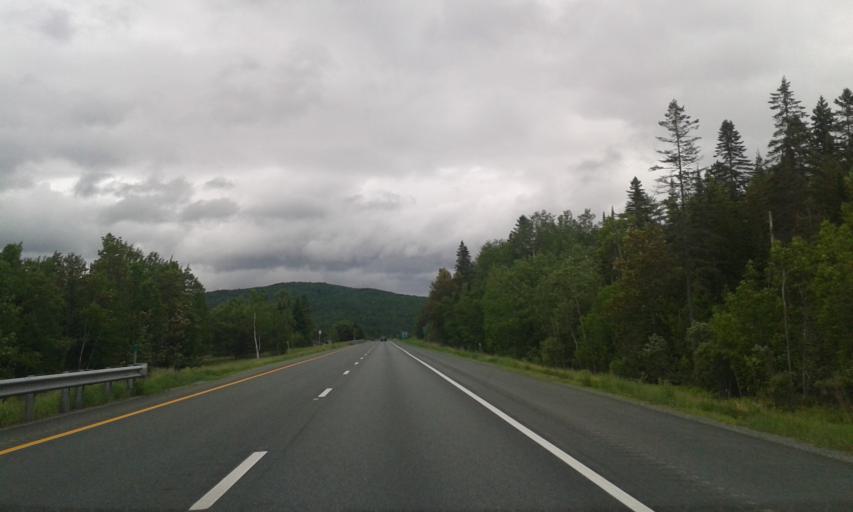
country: US
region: New Hampshire
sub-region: Grafton County
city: Littleton
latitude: 44.3224
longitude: -71.8195
